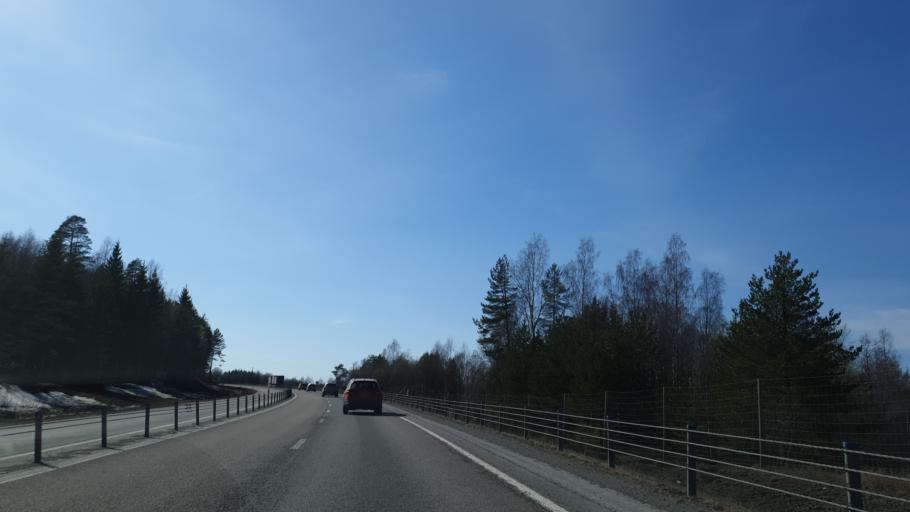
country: SE
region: Vaesternorrland
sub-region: Haernoesands Kommun
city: Haernoesand
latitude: 62.6131
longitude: 17.8496
